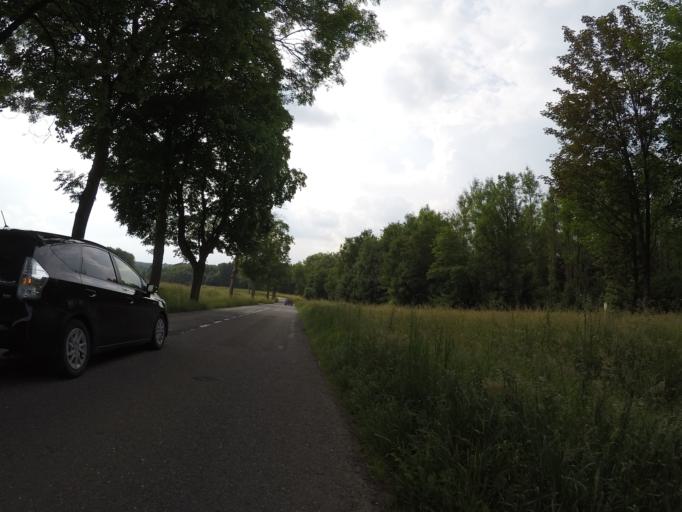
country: BE
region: Wallonia
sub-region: Province de Namur
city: Assesse
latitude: 50.3151
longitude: 5.0339
